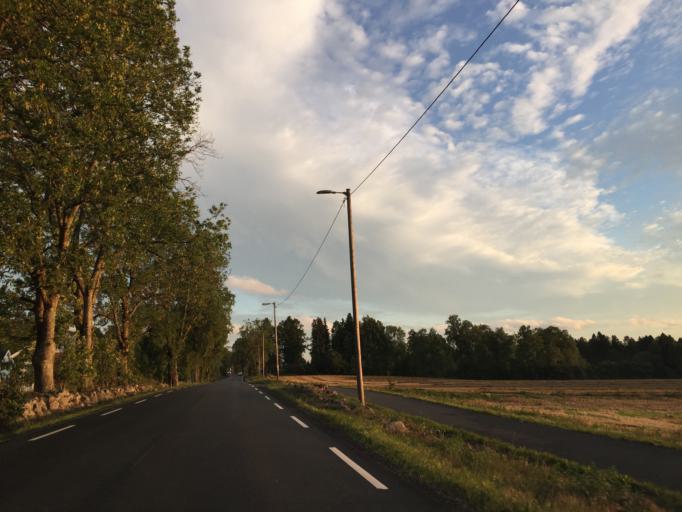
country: NO
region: Akershus
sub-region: As
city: As
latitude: 59.7130
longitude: 10.7733
